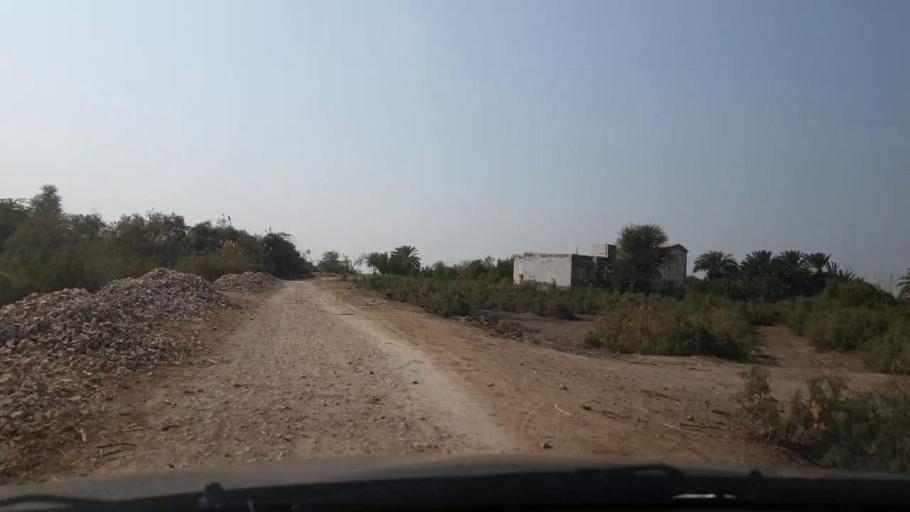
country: PK
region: Sindh
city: Jhol
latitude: 25.8983
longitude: 69.0088
